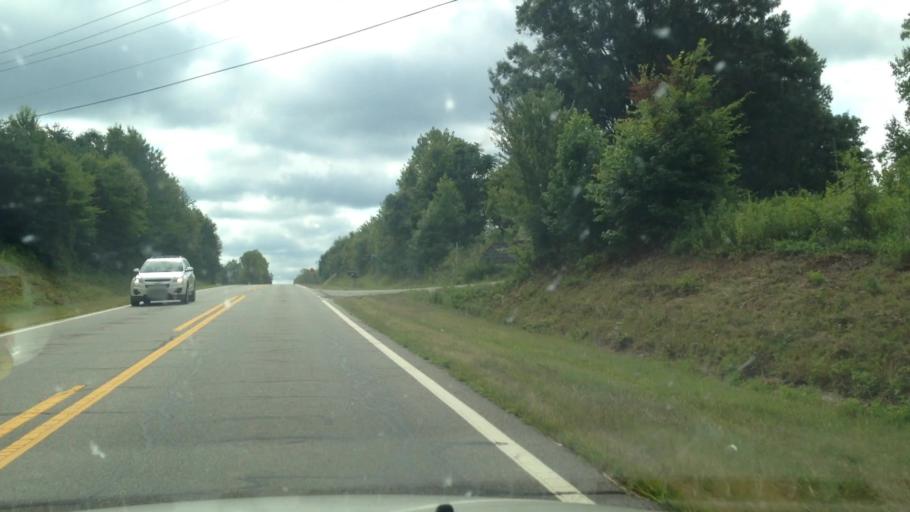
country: US
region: North Carolina
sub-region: Rockingham County
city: Madison
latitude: 36.3809
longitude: -79.9006
